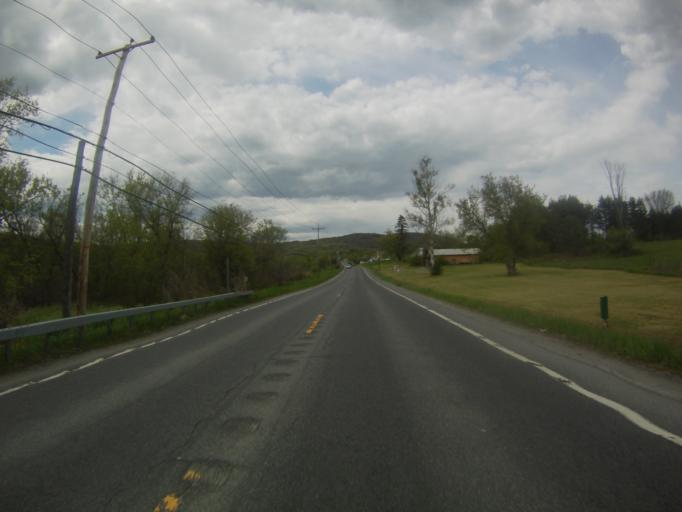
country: US
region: New York
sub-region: Essex County
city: Ticonderoga
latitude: 43.8736
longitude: -73.4450
